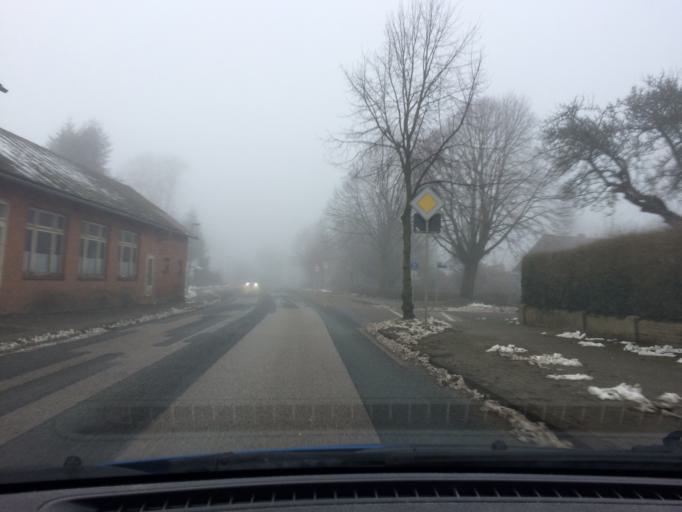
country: DE
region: Schleswig-Holstein
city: Kollow
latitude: 53.4670
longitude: 10.4620
